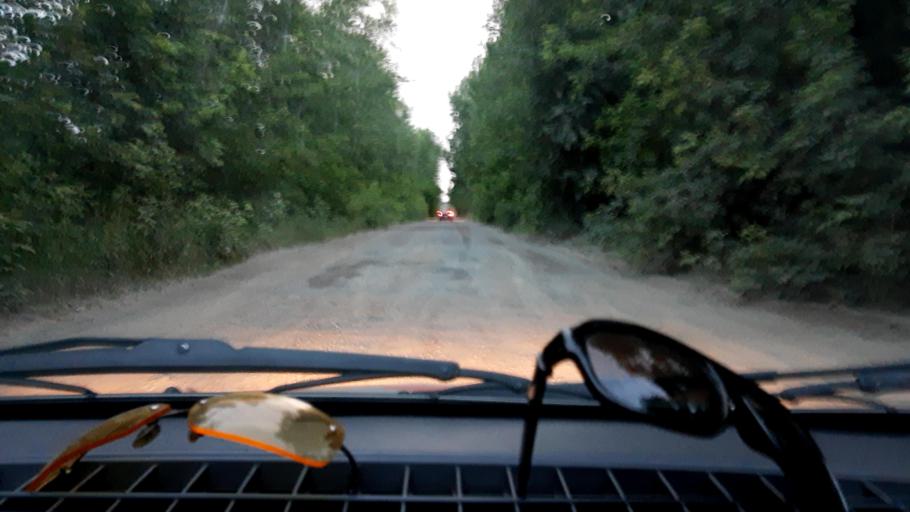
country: RU
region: Bashkortostan
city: Avdon
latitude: 54.6606
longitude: 55.8211
